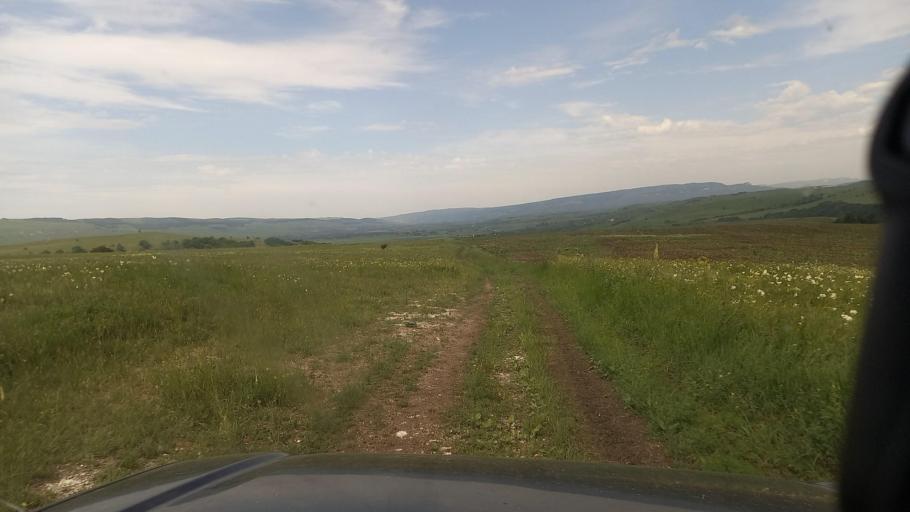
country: RU
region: Krasnodarskiy
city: Peredovaya
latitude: 44.0763
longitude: 41.3264
